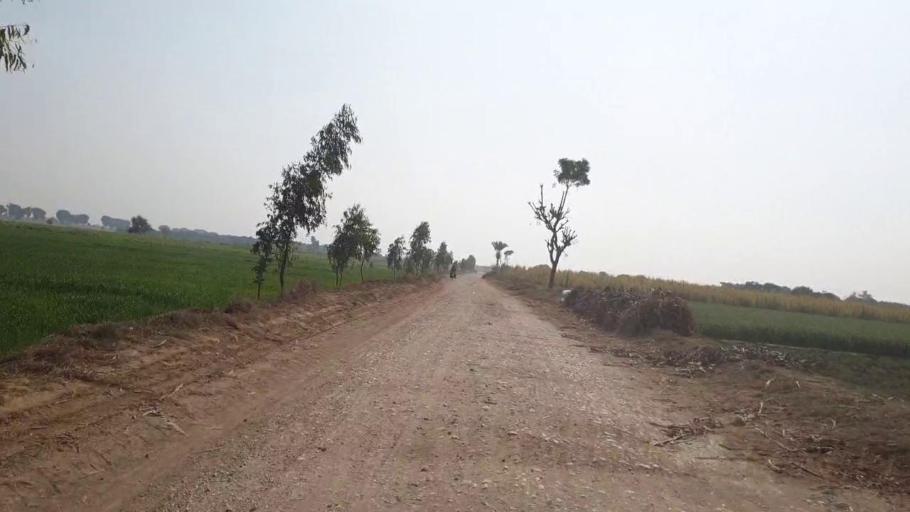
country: PK
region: Sindh
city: Bhit Shah
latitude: 25.7164
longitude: 68.5457
